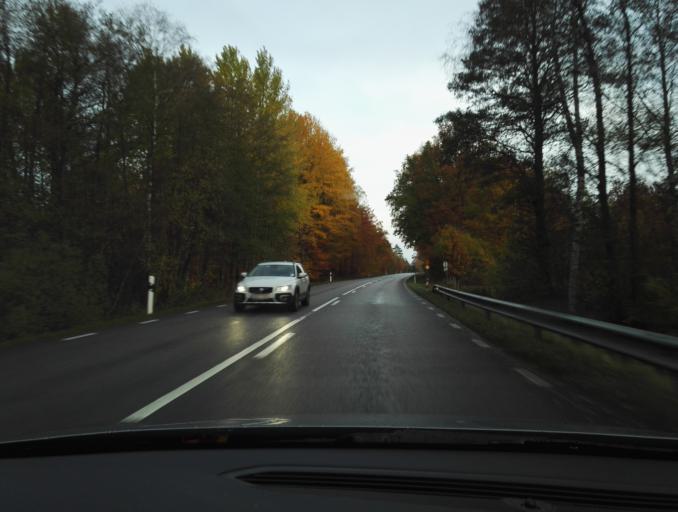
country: SE
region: Kronoberg
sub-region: Vaxjo Kommun
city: Gemla
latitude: 56.9653
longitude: 14.7116
